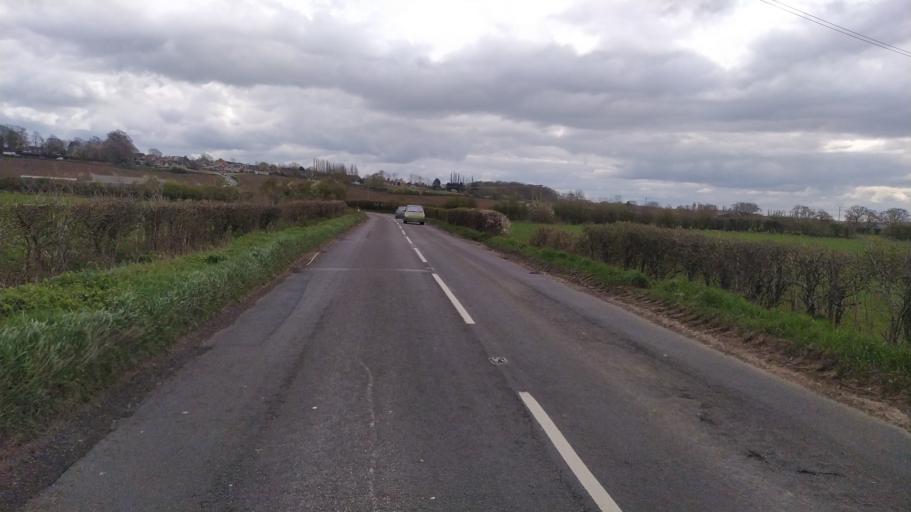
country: GB
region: England
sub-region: Wiltshire
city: North Bradley
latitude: 51.3063
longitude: -2.1838
